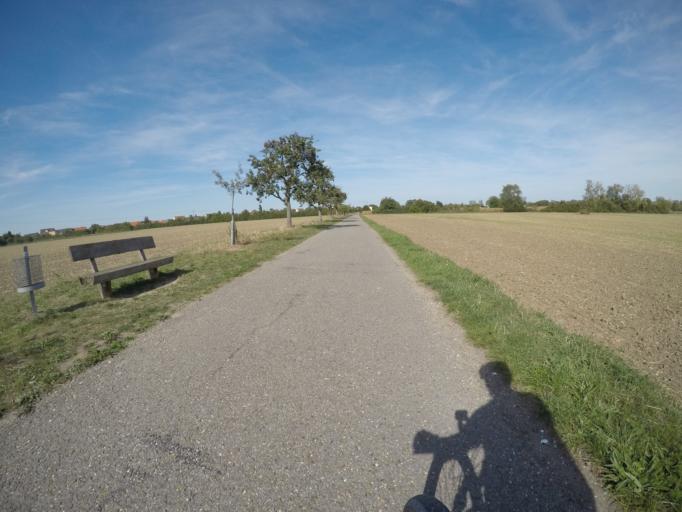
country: DE
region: Baden-Wuerttemberg
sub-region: Karlsruhe Region
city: Ubstadt-Weiher
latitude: 49.1730
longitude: 8.6217
